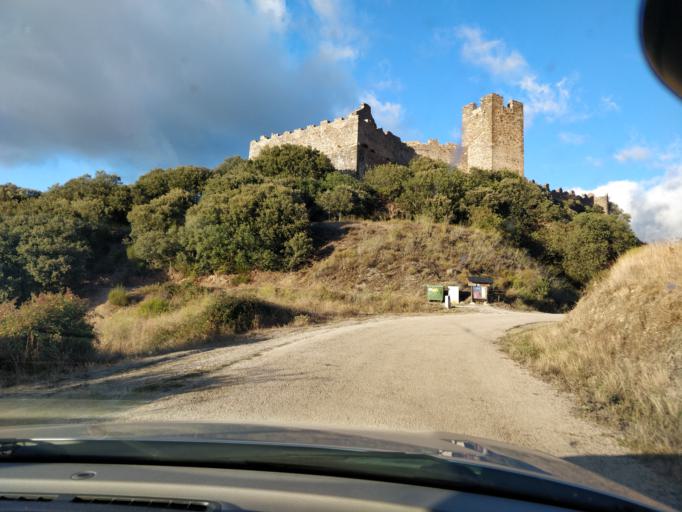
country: ES
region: Castille and Leon
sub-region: Provincia de Leon
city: Borrenes
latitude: 42.4871
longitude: -6.6941
